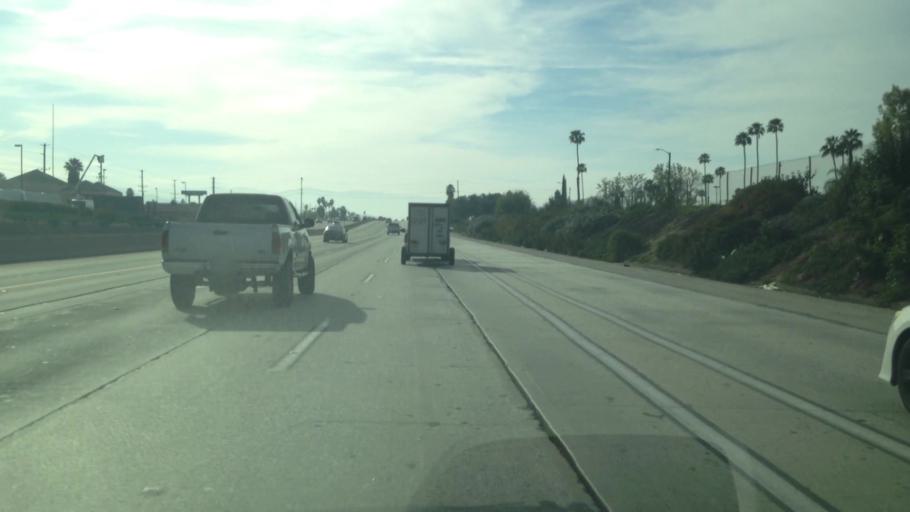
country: US
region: California
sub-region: Riverside County
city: Riverside
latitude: 33.9257
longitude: -117.4236
